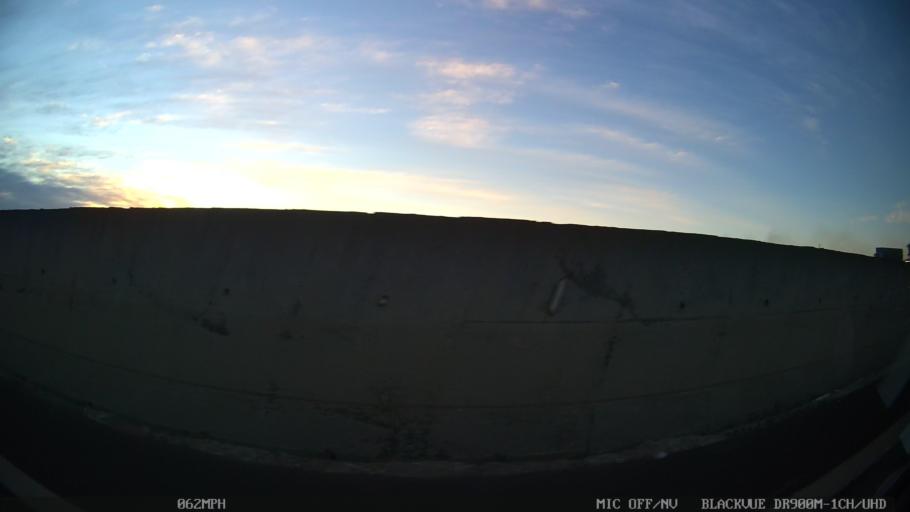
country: BR
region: Sao Paulo
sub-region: Catanduva
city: Catanduva
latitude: -21.1166
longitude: -48.9805
